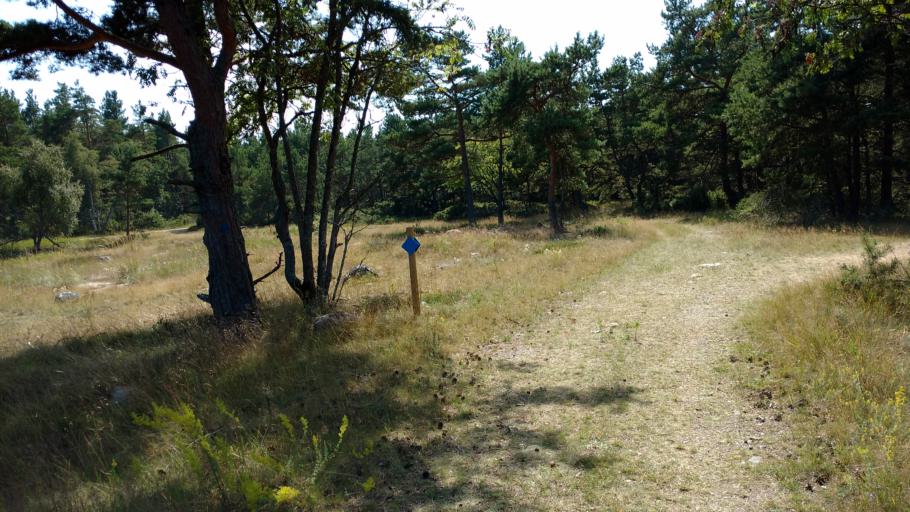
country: FI
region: Varsinais-Suomi
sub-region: Aboland-Turunmaa
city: Dragsfjaerd
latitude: 59.8074
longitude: 22.3153
